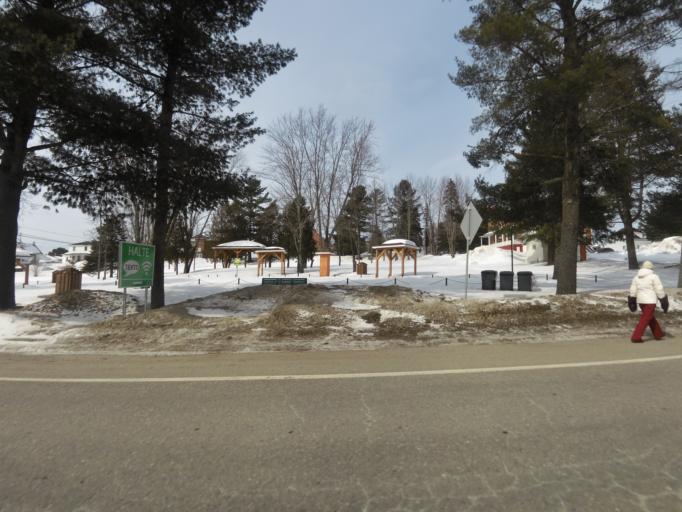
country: CA
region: Quebec
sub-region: Laurentides
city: Ferme-Neuve
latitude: 46.7801
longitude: -75.3356
